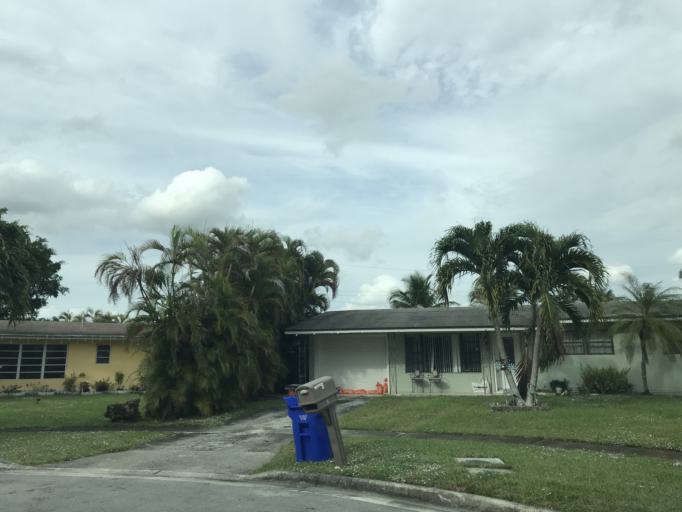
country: US
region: Florida
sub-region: Broward County
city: Margate
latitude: 26.2559
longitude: -80.2054
